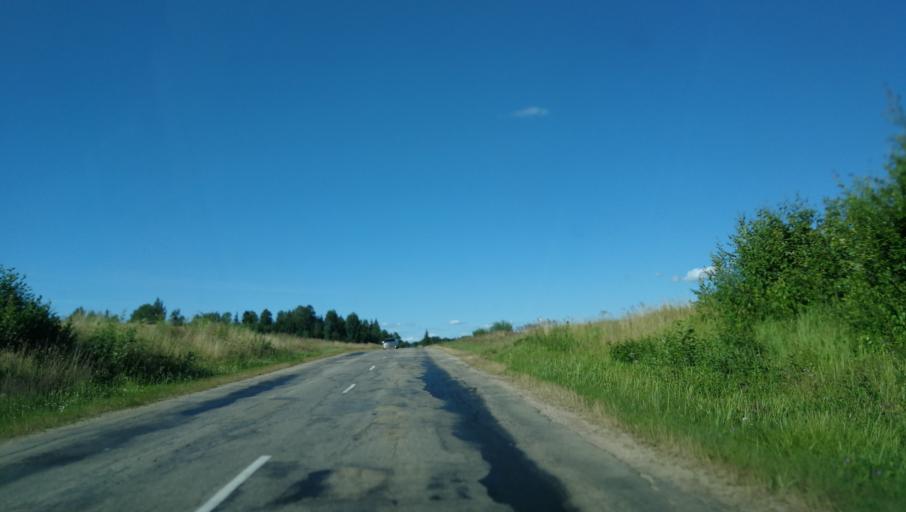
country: LV
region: Madonas Rajons
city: Madona
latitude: 56.9589
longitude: 26.0453
